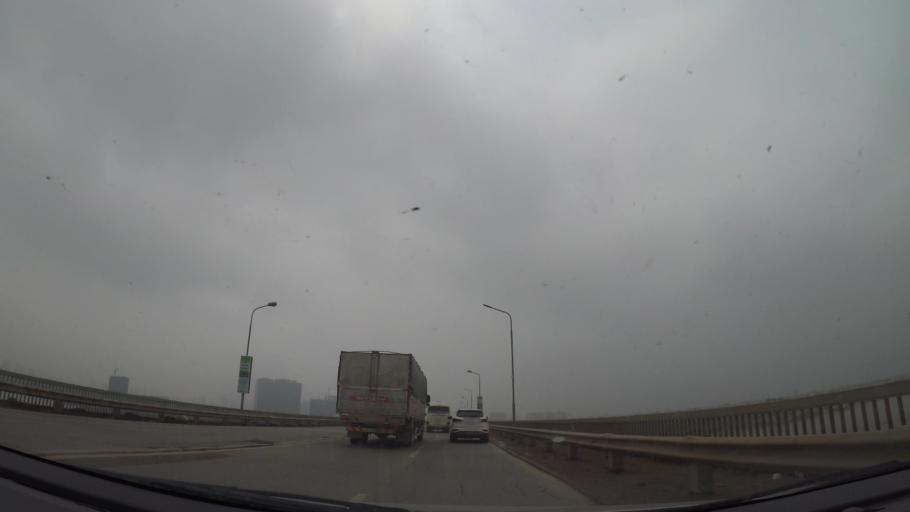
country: VN
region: Ha Noi
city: Tay Ho
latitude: 21.0987
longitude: 105.7864
